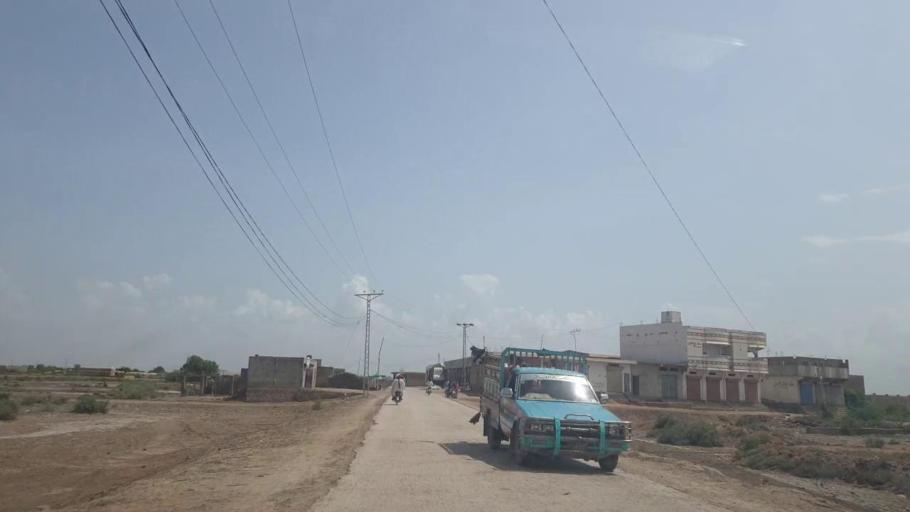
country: PK
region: Sindh
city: Naukot
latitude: 24.7590
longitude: 69.1972
